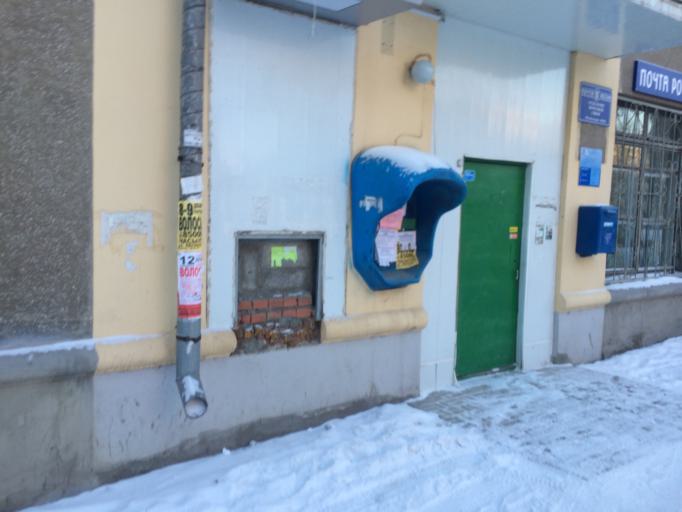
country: RU
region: Chelyabinsk
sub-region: Gorod Magnitogorsk
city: Magnitogorsk
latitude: 53.4150
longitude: 58.9853
